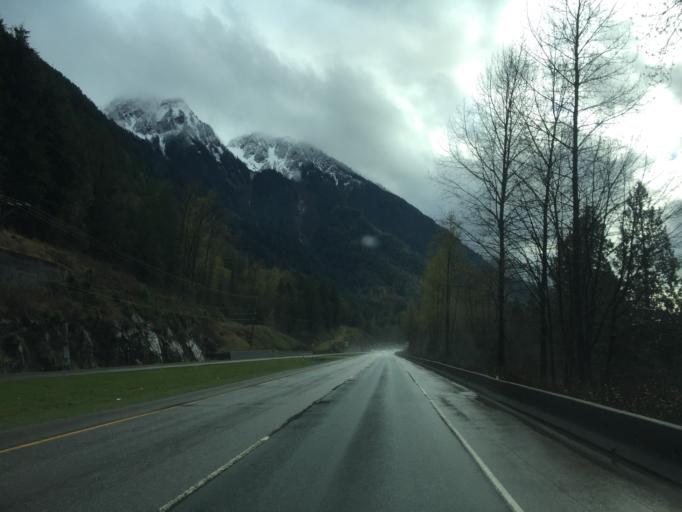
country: CA
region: British Columbia
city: Agassiz
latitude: 49.2244
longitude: -121.6878
